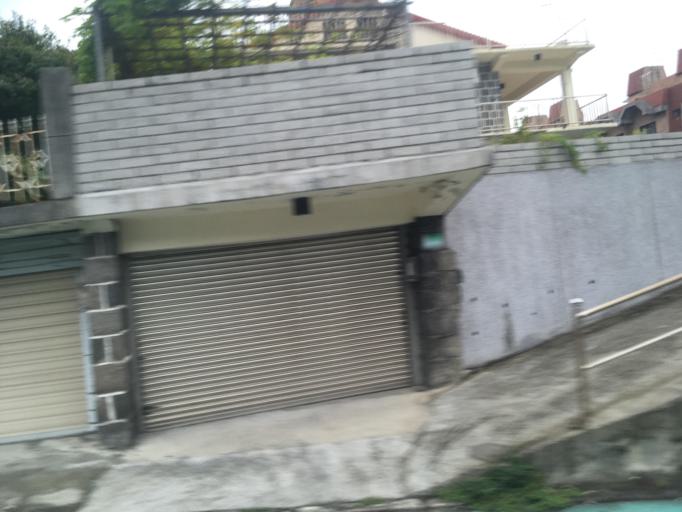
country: TW
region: Taipei
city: Taipei
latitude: 25.1317
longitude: 121.5283
